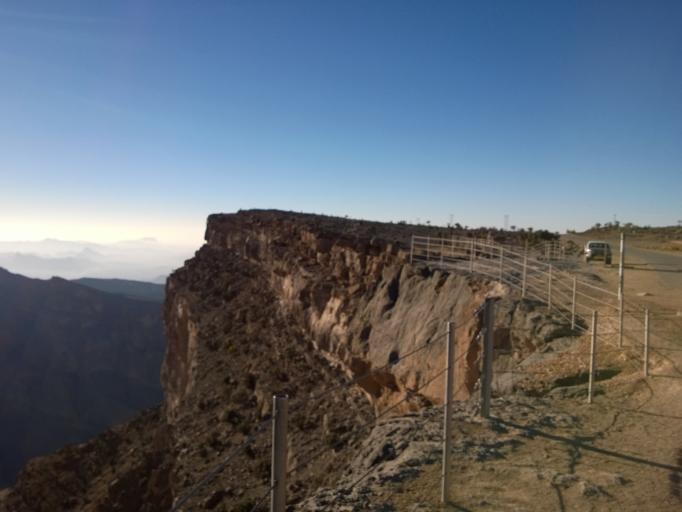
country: OM
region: Muhafazat ad Dakhiliyah
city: Bahla'
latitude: 23.2129
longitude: 57.2040
